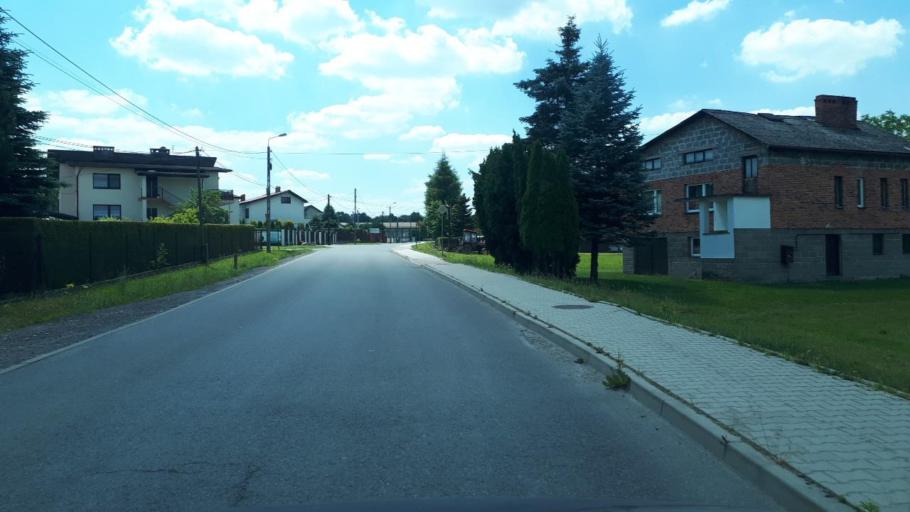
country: PL
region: Silesian Voivodeship
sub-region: Powiat bielski
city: Pisarzowice
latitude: 49.8792
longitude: 19.1432
